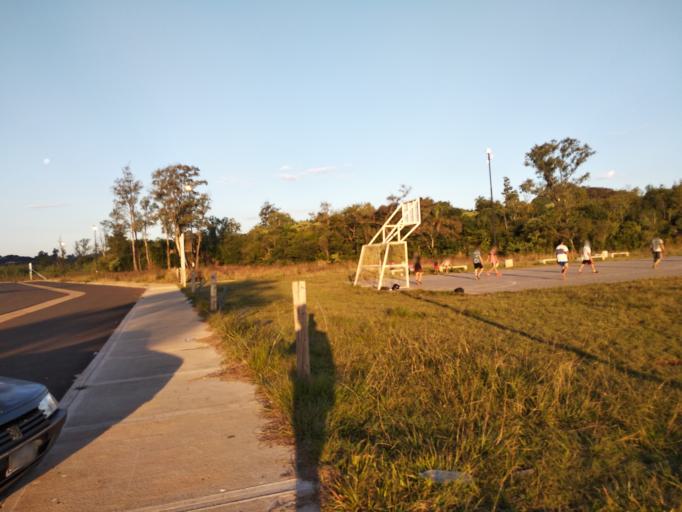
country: AR
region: Misiones
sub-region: Departamento de Capital
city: Posadas
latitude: -27.3958
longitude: -55.9554
